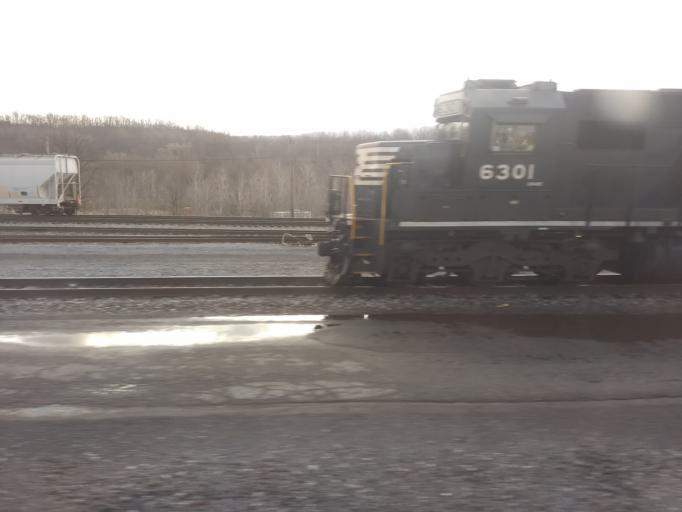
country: US
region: Pennsylvania
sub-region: Blair County
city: Greenwood
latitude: 40.5400
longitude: -78.3768
